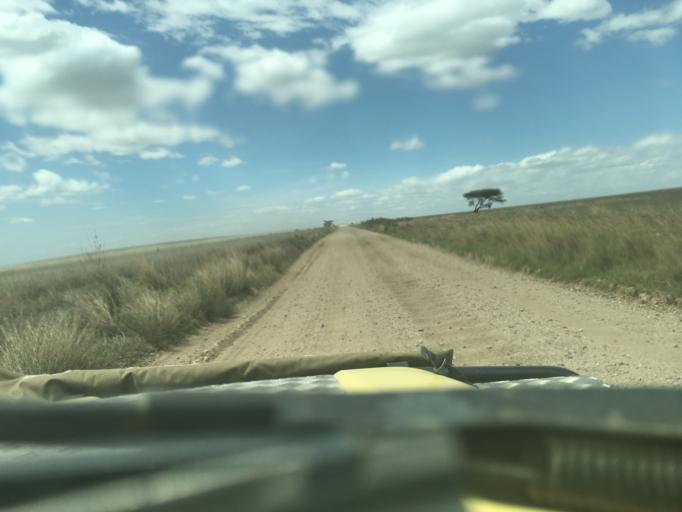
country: TZ
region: Mara
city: Mugumu
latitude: -2.5872
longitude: 34.8792
